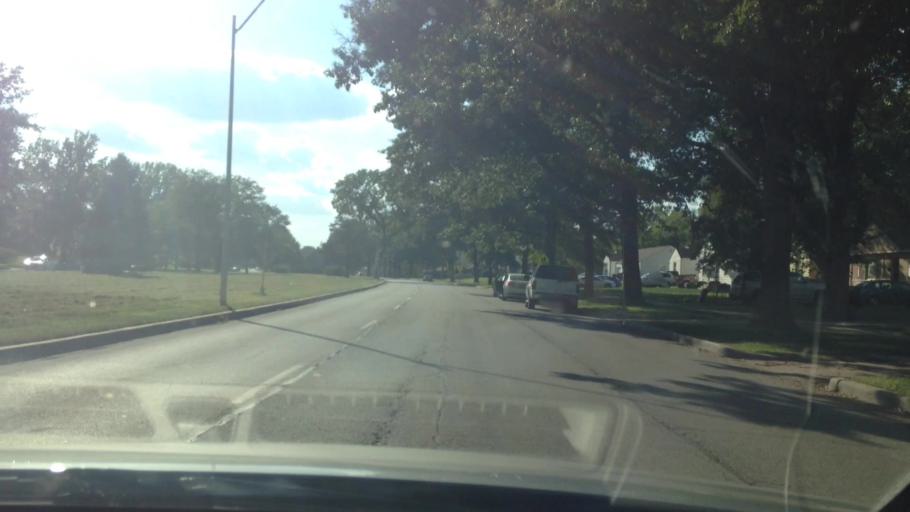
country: US
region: Kansas
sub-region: Johnson County
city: Mission Hills
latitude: 39.0079
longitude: -94.5499
